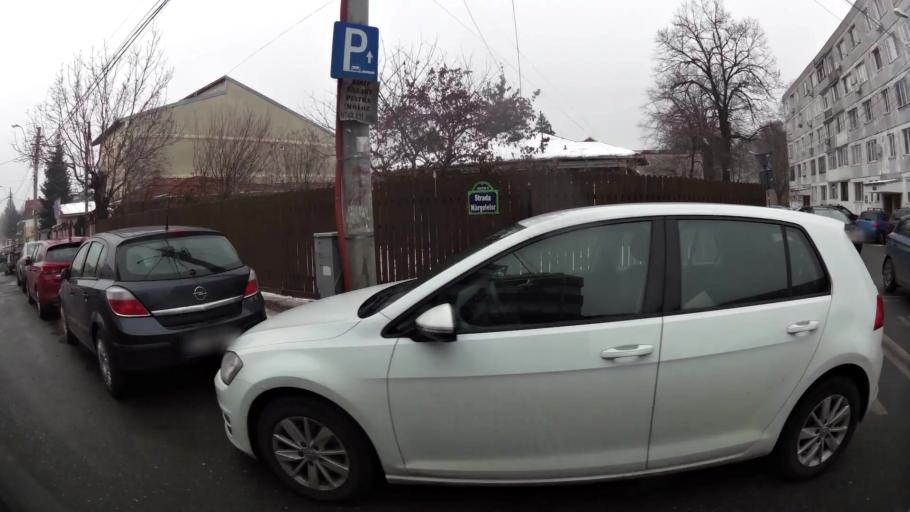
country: RO
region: Ilfov
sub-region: Comuna Chiajna
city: Rosu
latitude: 44.4367
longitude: 26.0089
